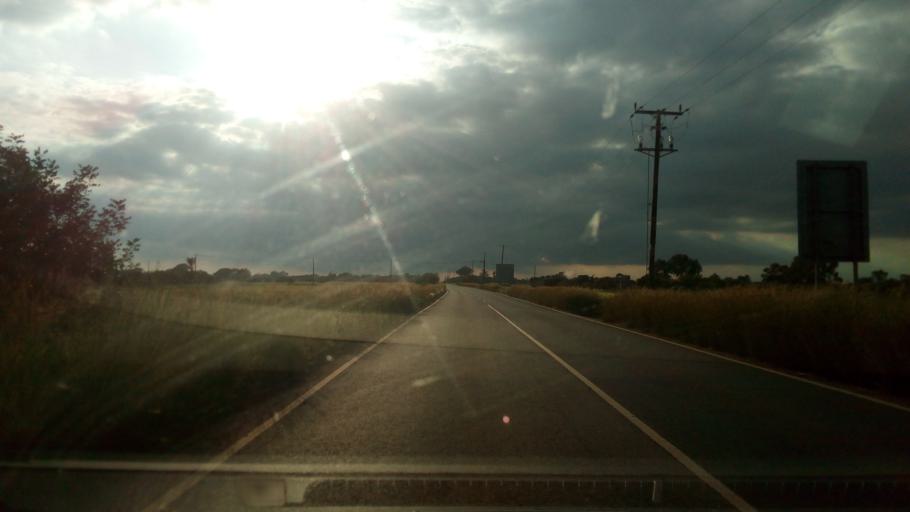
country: CY
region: Ammochostos
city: Liopetri
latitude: 34.9760
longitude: 33.8726
